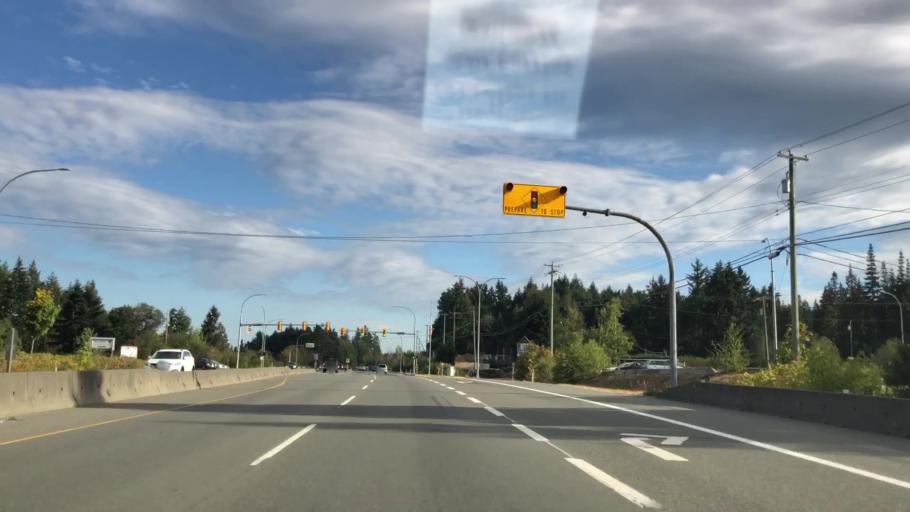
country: CA
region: British Columbia
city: North Saanich
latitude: 48.6431
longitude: -123.5549
